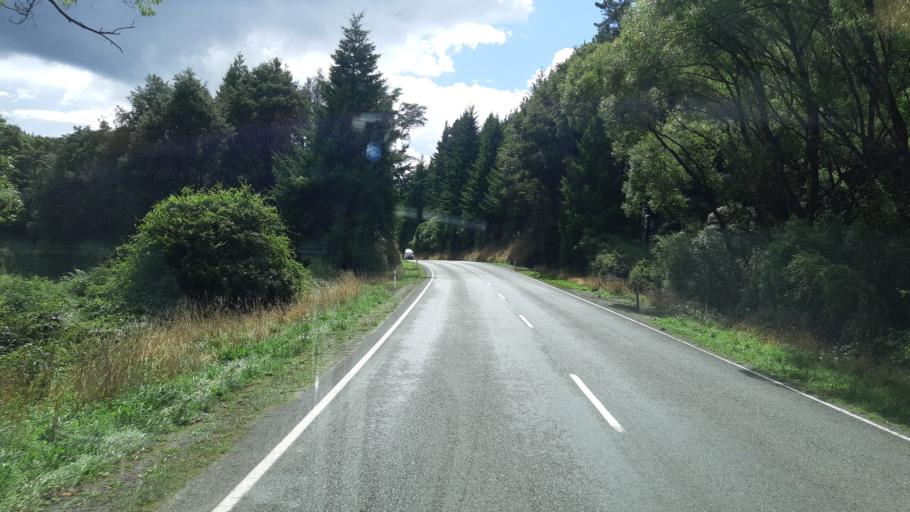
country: NZ
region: Tasman
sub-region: Tasman District
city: Wakefield
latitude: -41.5841
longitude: 172.7666
